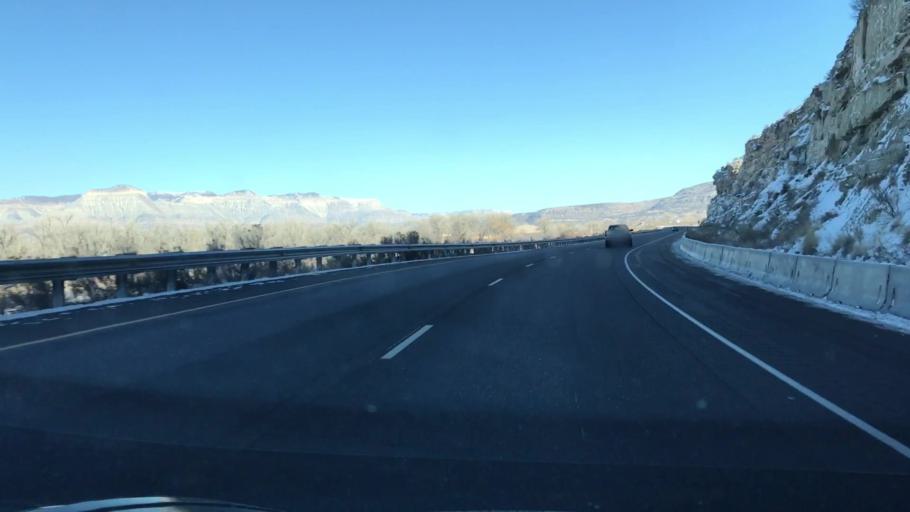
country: US
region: Colorado
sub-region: Mesa County
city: Palisade
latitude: 39.2772
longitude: -108.2412
